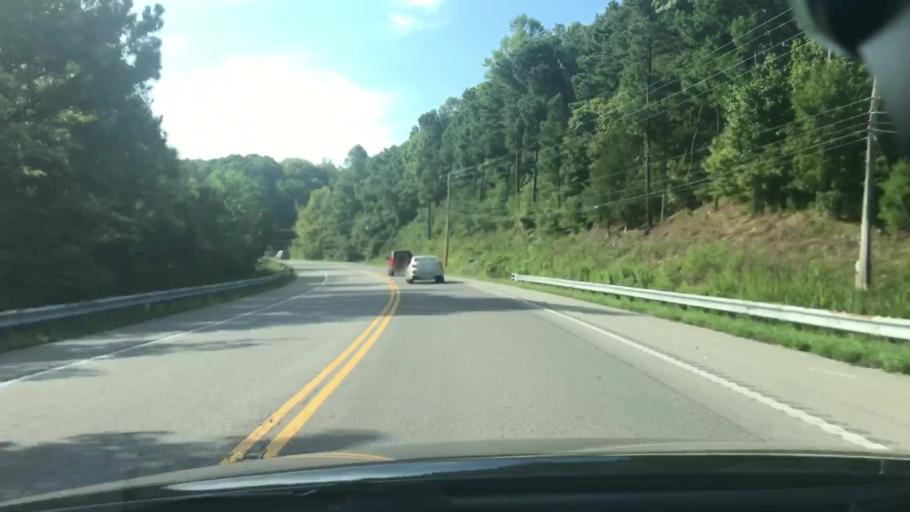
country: US
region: Tennessee
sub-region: Williamson County
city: Franklin
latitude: 35.9667
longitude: -86.9692
